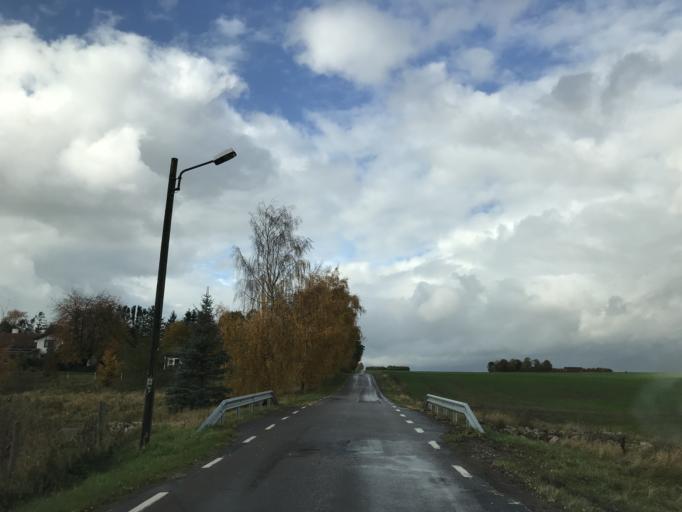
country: SE
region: Skane
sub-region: Svalovs Kommun
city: Svaloev
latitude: 55.9032
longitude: 13.1811
